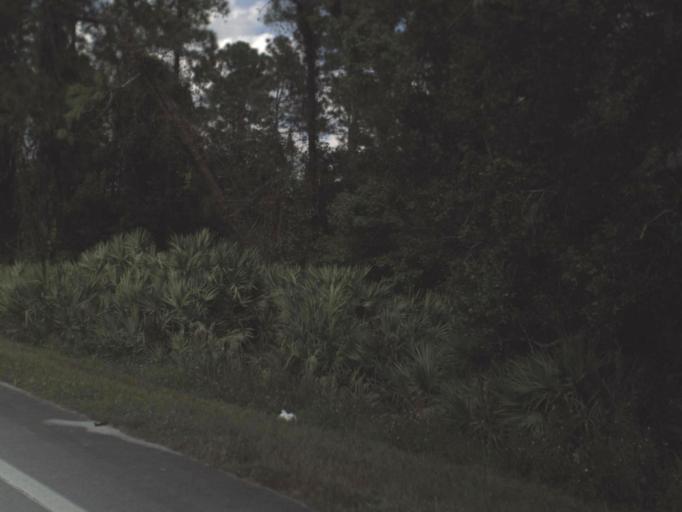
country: US
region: Florida
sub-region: Indian River County
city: Fellsmere
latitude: 27.5805
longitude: -80.8355
